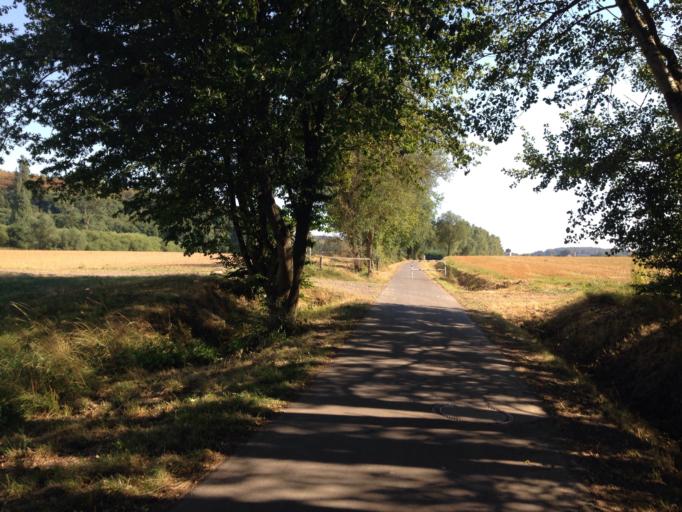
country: DE
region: Hesse
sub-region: Regierungsbezirk Giessen
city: Rabenau
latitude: 50.6561
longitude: 8.8923
